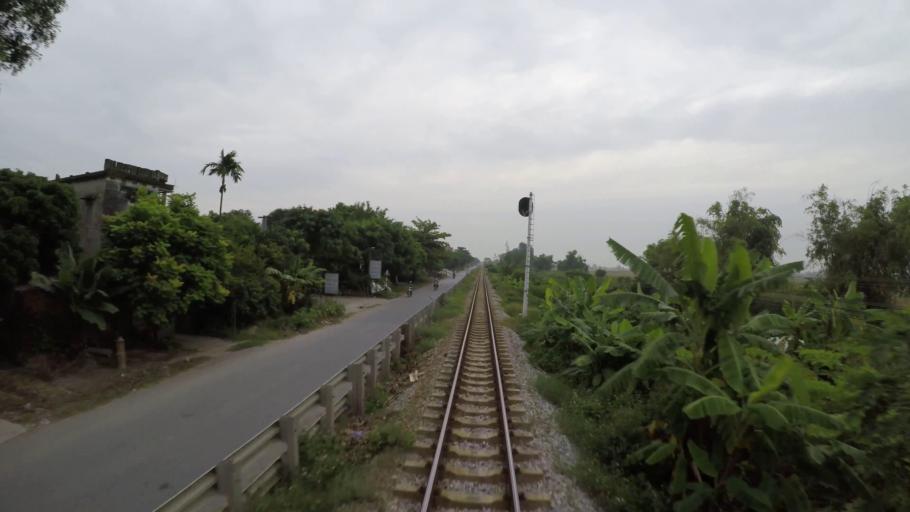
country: VN
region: Hung Yen
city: Ban Yen Nhan
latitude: 20.9687
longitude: 106.1044
